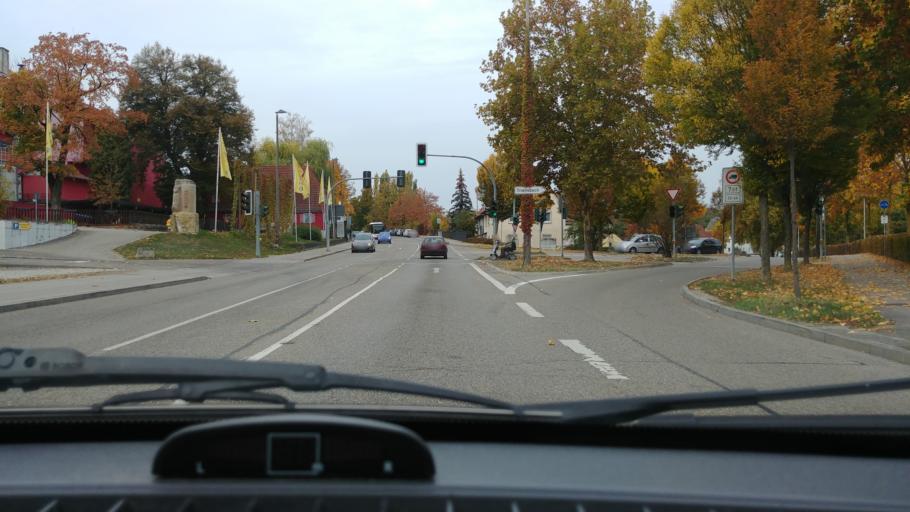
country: DE
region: Baden-Wuerttemberg
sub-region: Regierungsbezirk Stuttgart
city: Crailsheim
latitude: 49.1417
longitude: 10.0595
